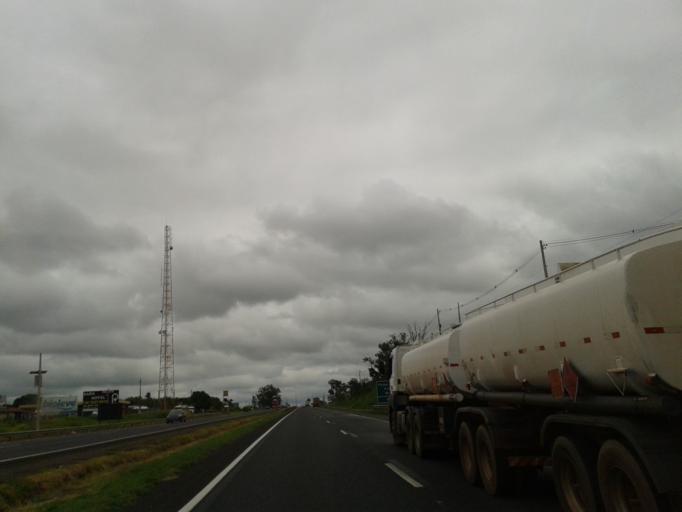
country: BR
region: Minas Gerais
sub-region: Uberlandia
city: Uberlandia
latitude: -18.9470
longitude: -48.2181
